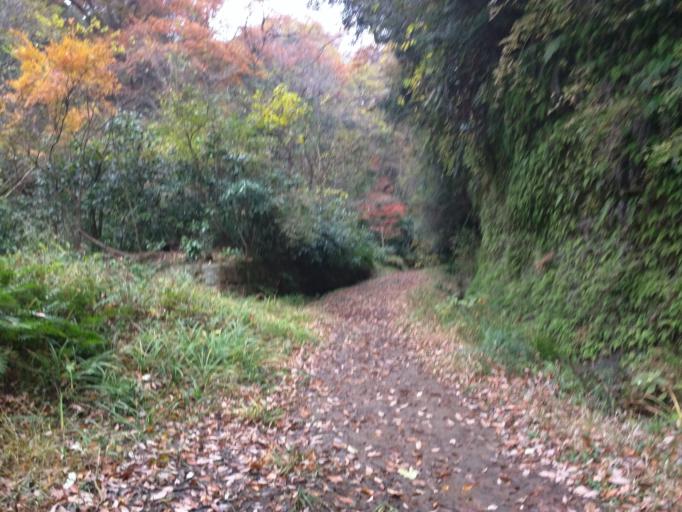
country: JP
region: Kanagawa
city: Zushi
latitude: 35.3260
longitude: 139.5875
